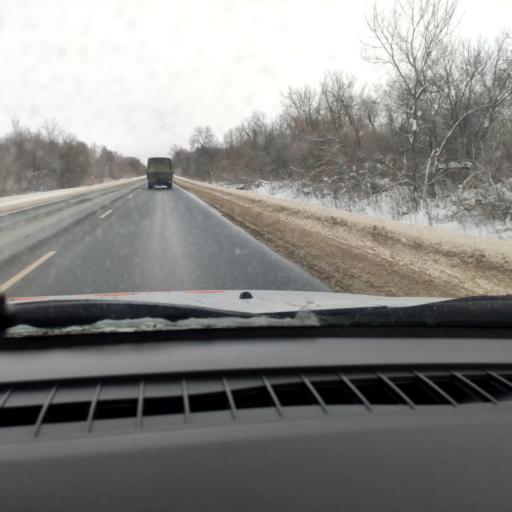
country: RU
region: Samara
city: Dubovyy Umet
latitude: 52.9536
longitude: 50.3066
